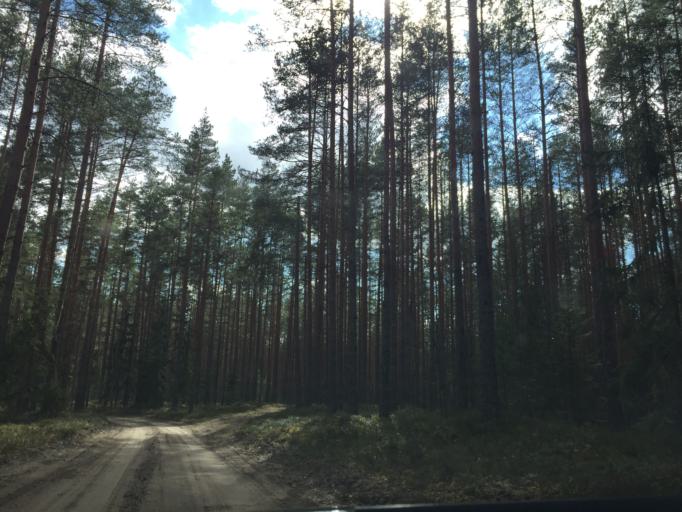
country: LV
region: Gulbenes Rajons
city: Gulbene
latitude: 57.2724
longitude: 26.5502
